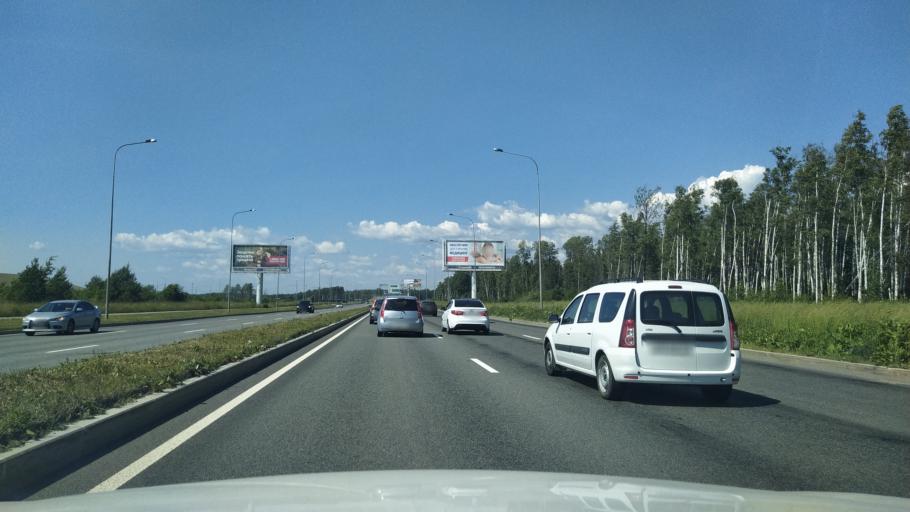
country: RU
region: St.-Petersburg
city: Levashovo
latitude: 60.0681
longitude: 30.1886
